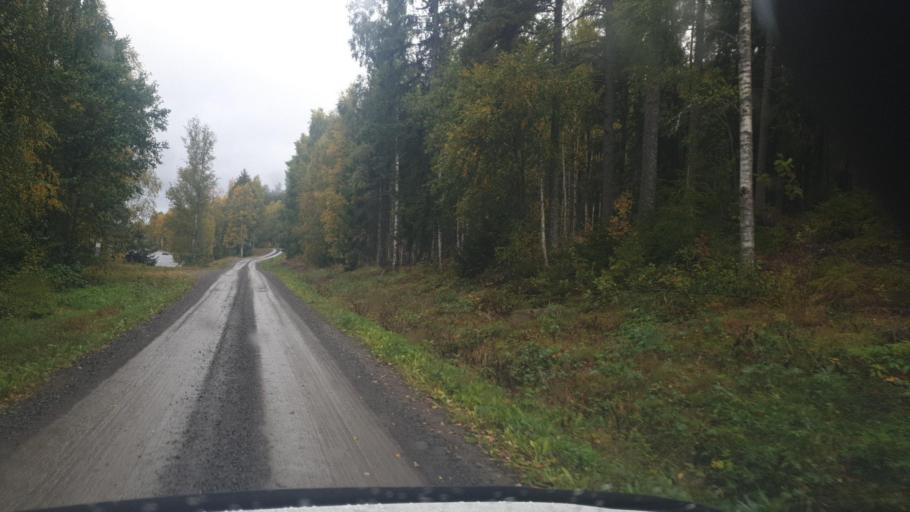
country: SE
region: Vaermland
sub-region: Arvika Kommun
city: Arvika
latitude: 59.8670
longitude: 12.8148
